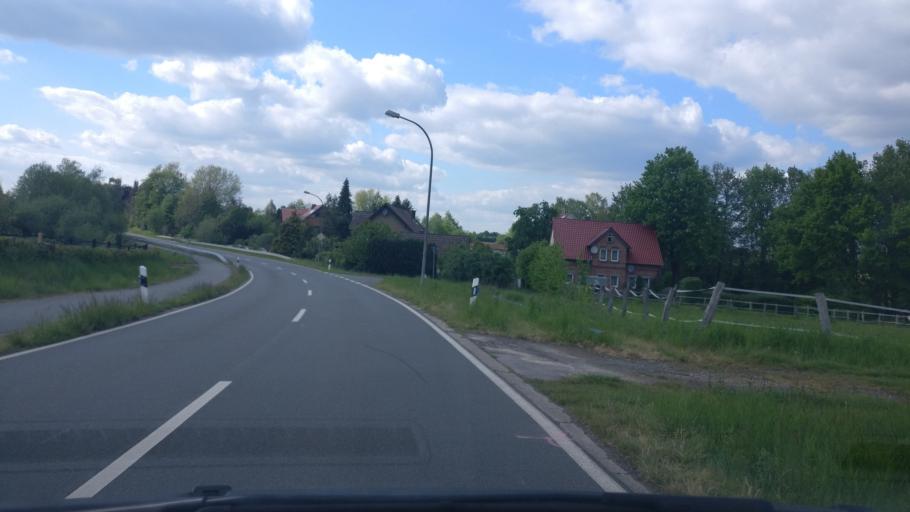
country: DE
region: North Rhine-Westphalia
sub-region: Regierungsbezirk Detmold
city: Leopoldshohe
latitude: 52.0031
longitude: 8.7281
